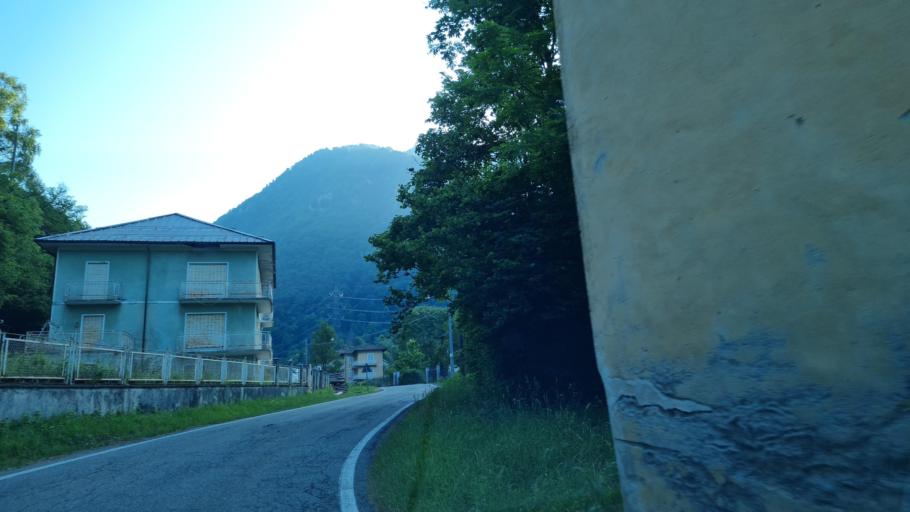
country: IT
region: Piedmont
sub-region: Provincia di Torino
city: Ronco Canavese
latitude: 45.5046
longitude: 7.5492
